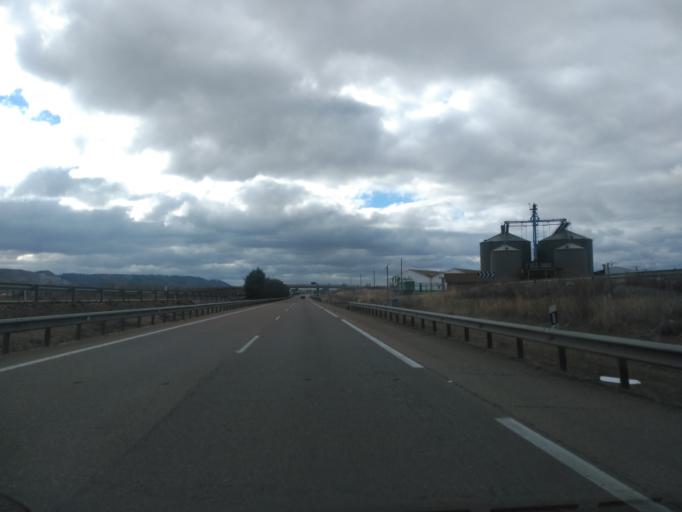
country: ES
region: Castille and Leon
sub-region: Provincia de Valladolid
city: Cubillas de Santa Marta
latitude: 41.7814
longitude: -4.6136
